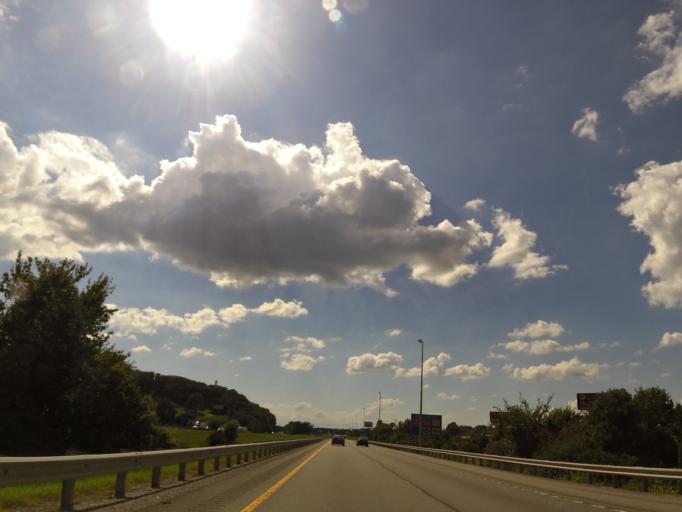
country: US
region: Tennessee
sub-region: Putnam County
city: Cookeville
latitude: 36.1361
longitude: -85.5086
